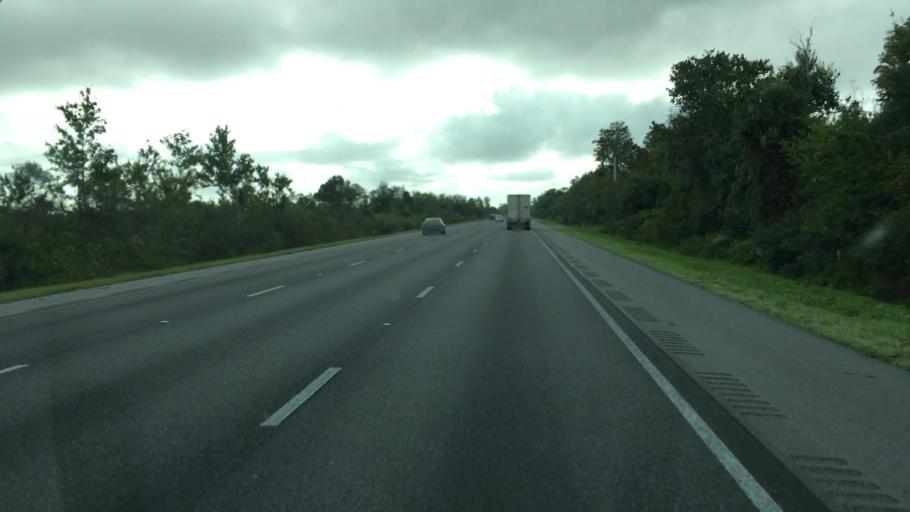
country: US
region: Florida
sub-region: Volusia County
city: Glencoe
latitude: 29.0357
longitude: -81.0032
